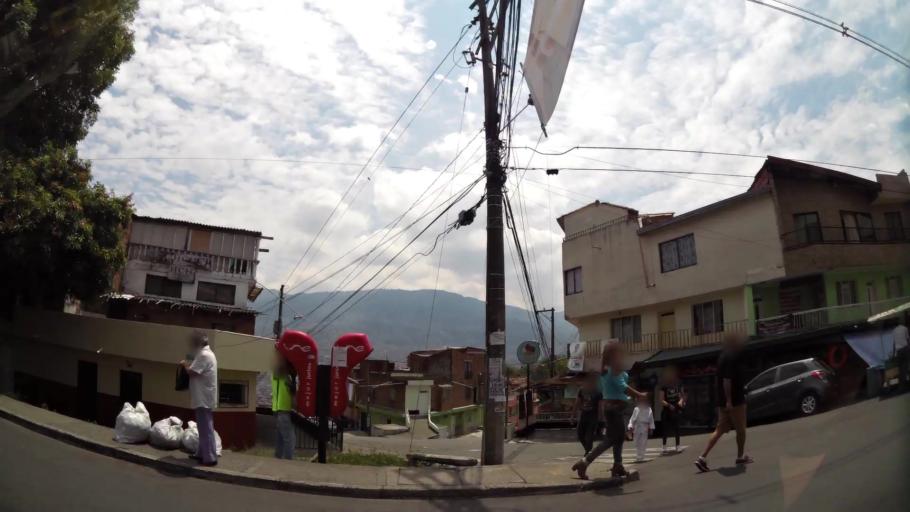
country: CO
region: Antioquia
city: Bello
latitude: 6.3036
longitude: -75.5708
